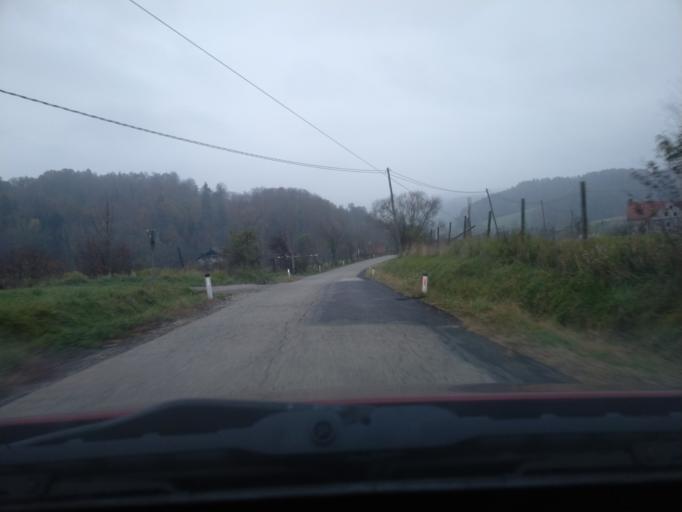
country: SI
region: Kungota
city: Zgornja Kungota
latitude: 46.6748
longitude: 15.6115
